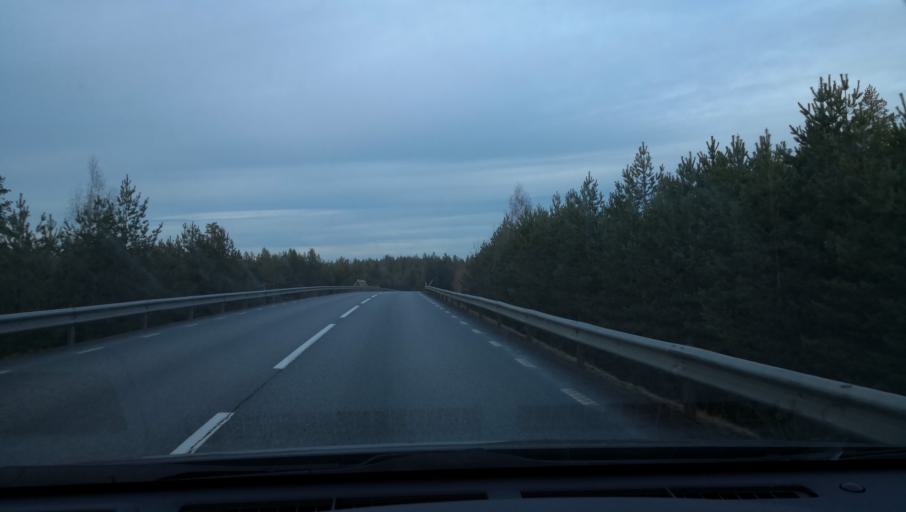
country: SE
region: OErebro
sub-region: Laxa Kommun
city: Laxa
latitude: 59.1203
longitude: 14.5836
